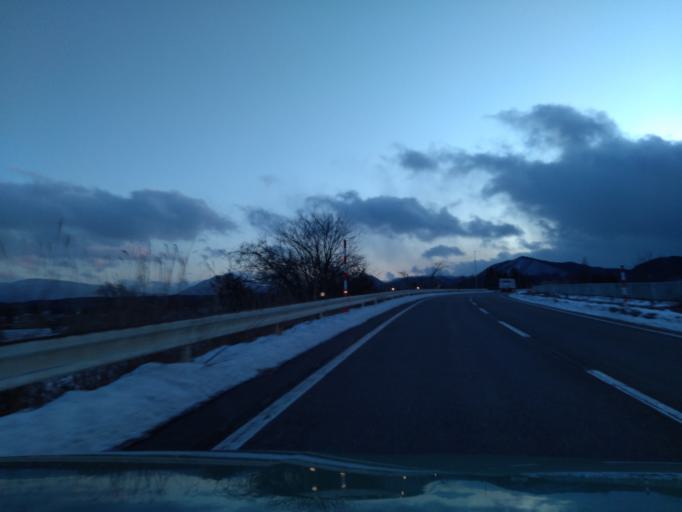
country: JP
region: Iwate
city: Shizukuishi
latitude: 39.6945
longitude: 140.9360
